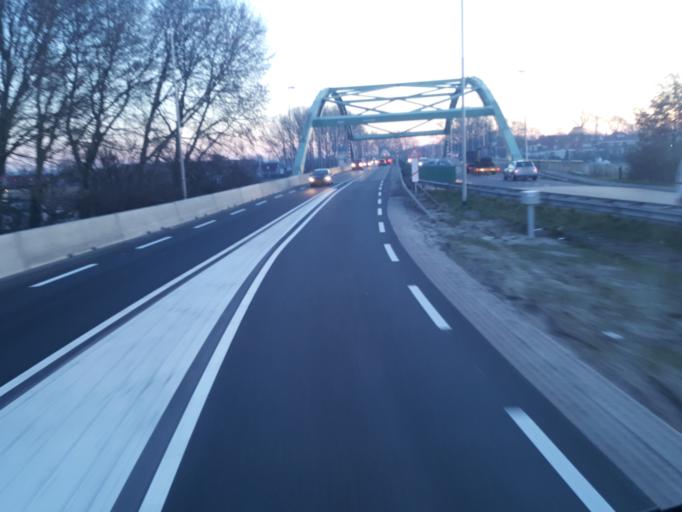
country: NL
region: Overijssel
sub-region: Gemeente Zwartewaterland
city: Hasselt
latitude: 52.5910
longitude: 6.0834
